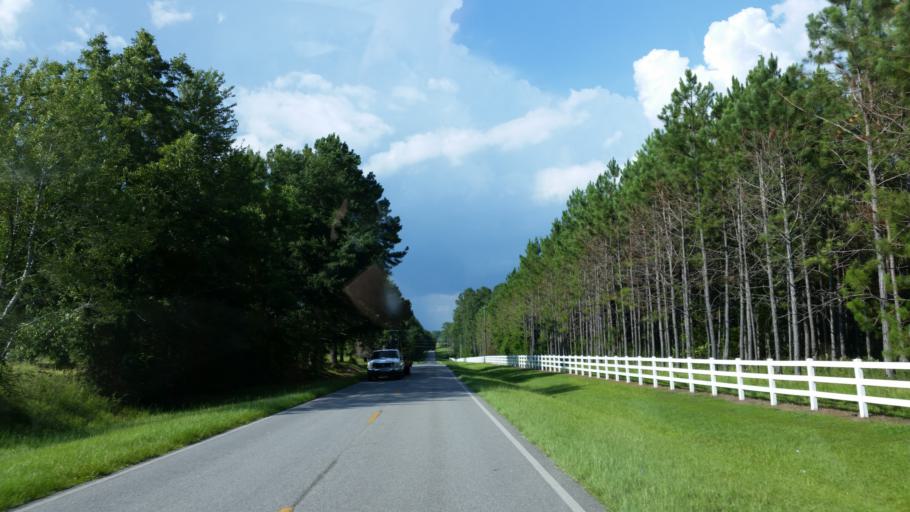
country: US
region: Georgia
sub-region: Lowndes County
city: Hahira
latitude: 30.9611
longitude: -83.4052
